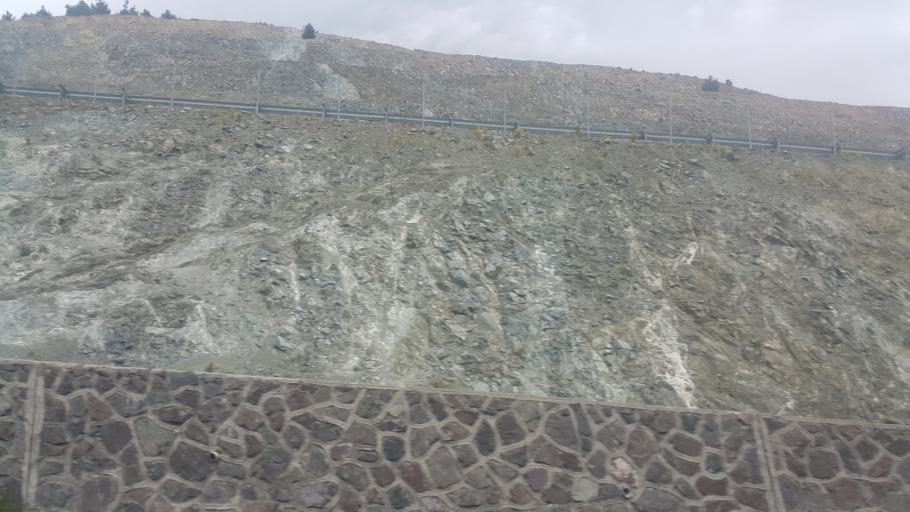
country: TR
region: Adana
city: Pozanti
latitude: 37.4205
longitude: 34.8769
